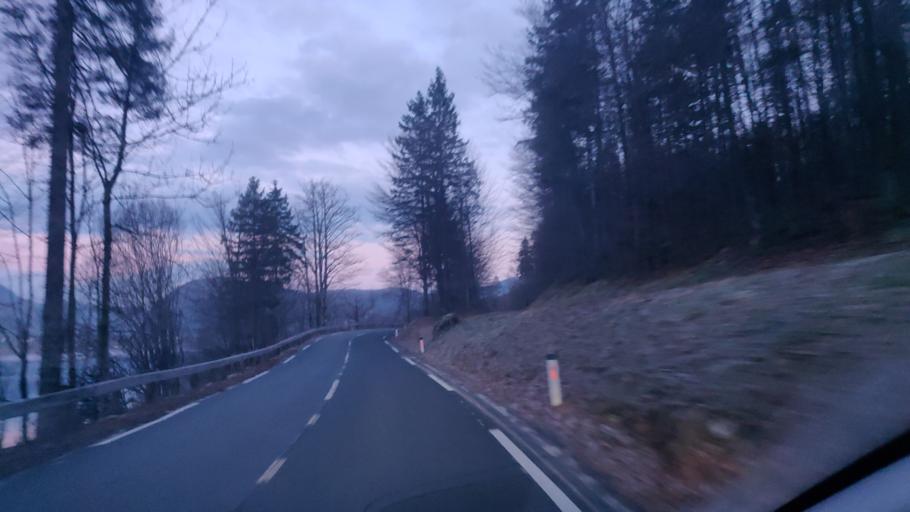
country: SI
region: Bohinj
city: Bohinjska Bistrica
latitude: 46.2800
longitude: 13.8562
